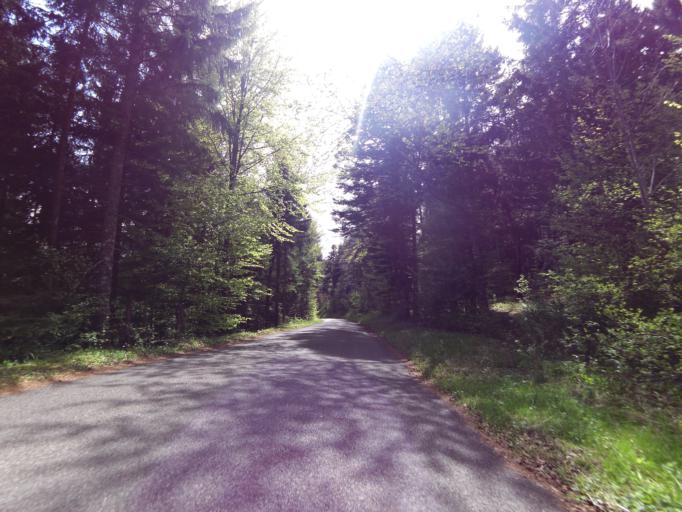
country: CH
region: Vaud
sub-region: Nyon District
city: Le Vaud
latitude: 46.4766
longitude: 6.2176
